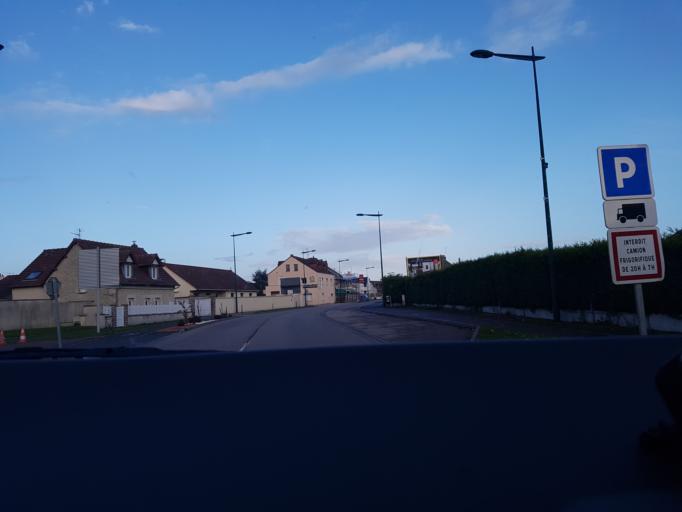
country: FR
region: Lower Normandy
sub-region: Departement du Calvados
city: Giberville
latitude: 49.1724
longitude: -0.2817
